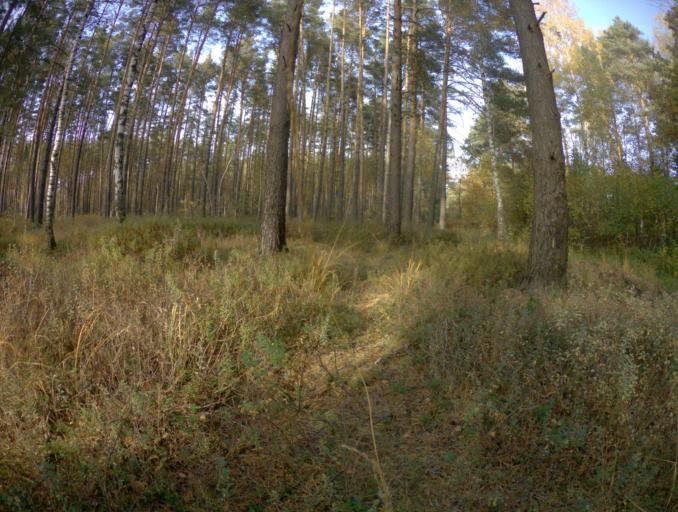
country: RU
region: Vladimir
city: Sobinka
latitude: 55.9924
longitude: 40.0579
